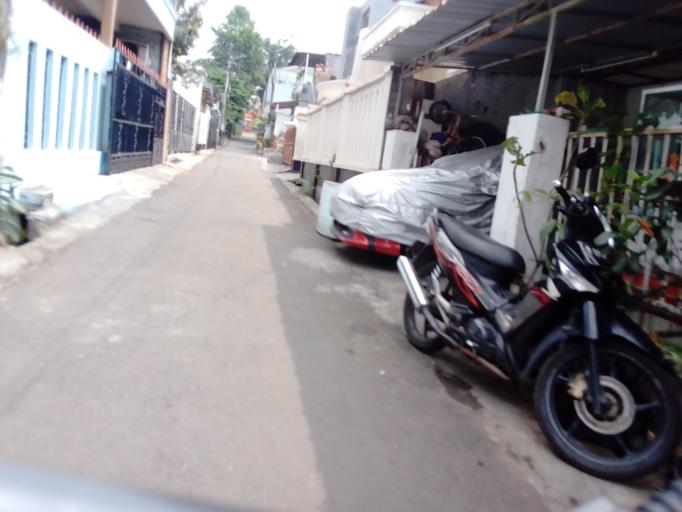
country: ID
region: Jakarta Raya
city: Jakarta
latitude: -6.2156
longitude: 106.8130
